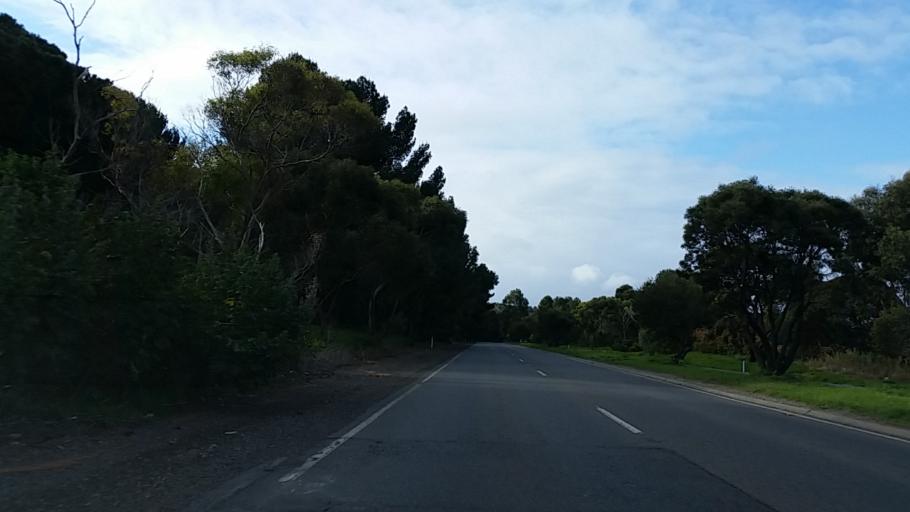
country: AU
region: South Australia
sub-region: Onkaparinga
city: Reynella
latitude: -35.0931
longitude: 138.5368
